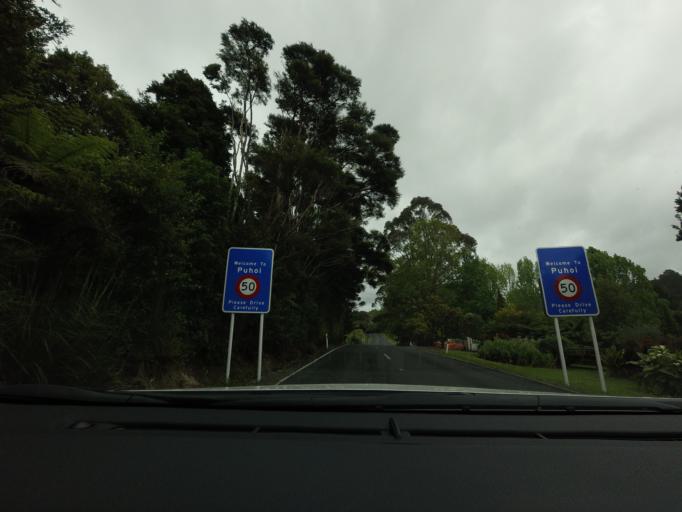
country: NZ
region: Auckland
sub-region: Auckland
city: Warkworth
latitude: -36.5165
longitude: 174.6653
